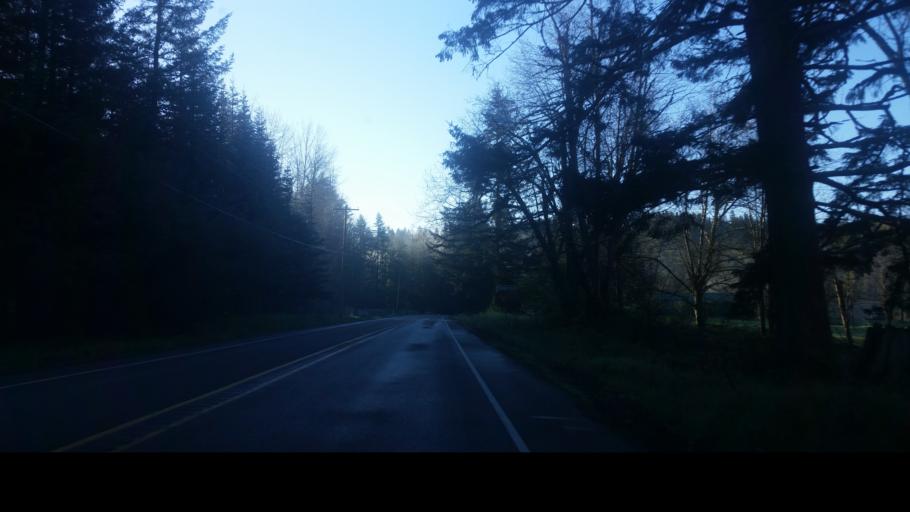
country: US
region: Washington
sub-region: Pierce County
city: Eatonville
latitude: 46.9437
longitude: -122.2847
